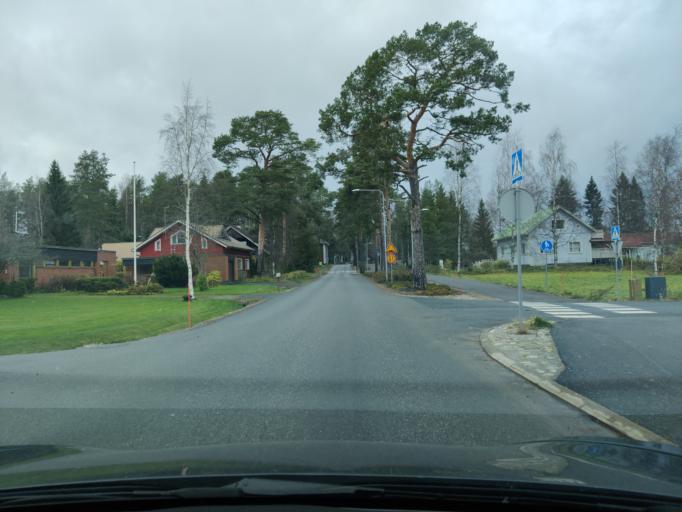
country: FI
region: Northern Savo
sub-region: Ylae-Savo
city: Kiuruvesi
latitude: 63.6495
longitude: 26.6345
